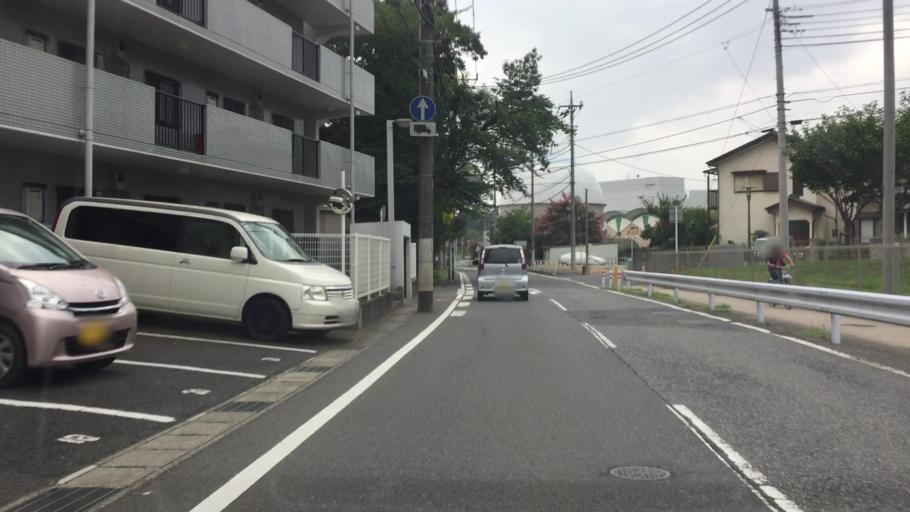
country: JP
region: Chiba
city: Matsudo
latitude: 35.8021
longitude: 139.9446
